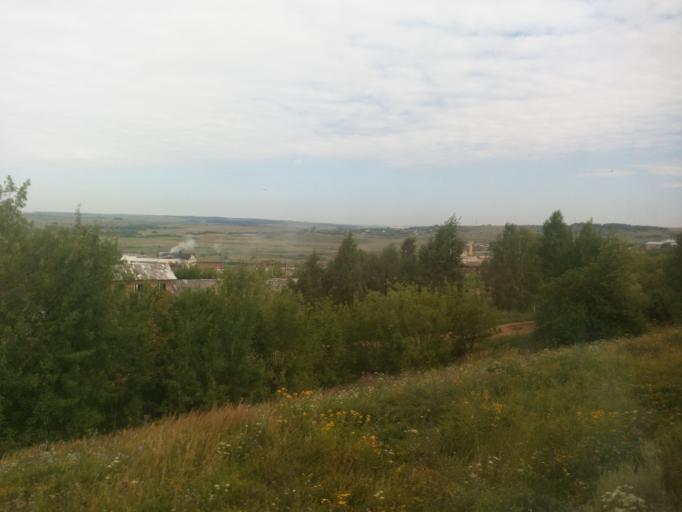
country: RU
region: Tatarstan
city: Mendeleyevsk
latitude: 55.9007
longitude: 52.3317
